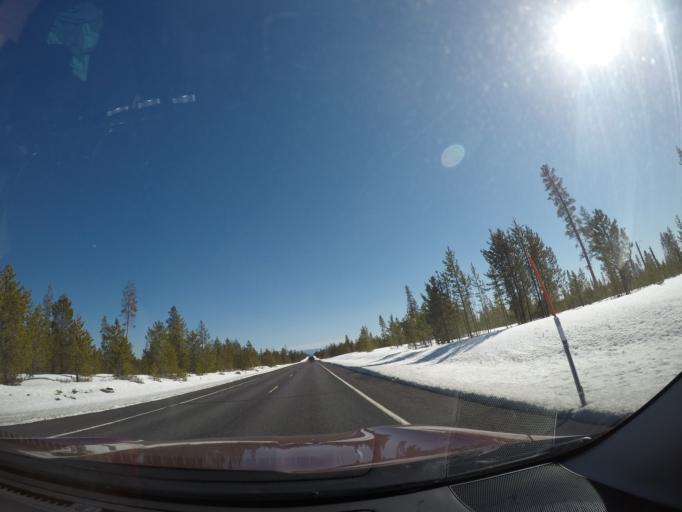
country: US
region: Oregon
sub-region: Deschutes County
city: Three Rivers
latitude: 43.8835
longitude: -121.5730
